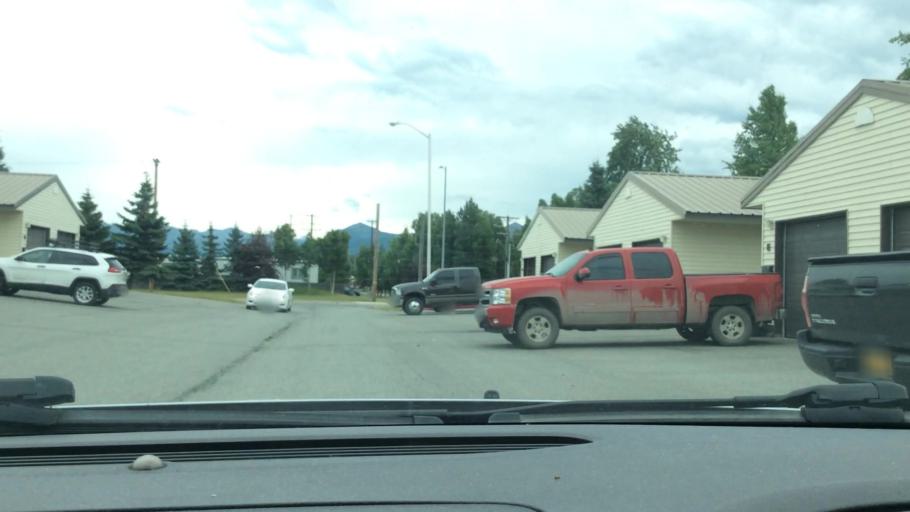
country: US
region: Alaska
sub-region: Anchorage Municipality
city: Anchorage
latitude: 61.2303
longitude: -149.8506
